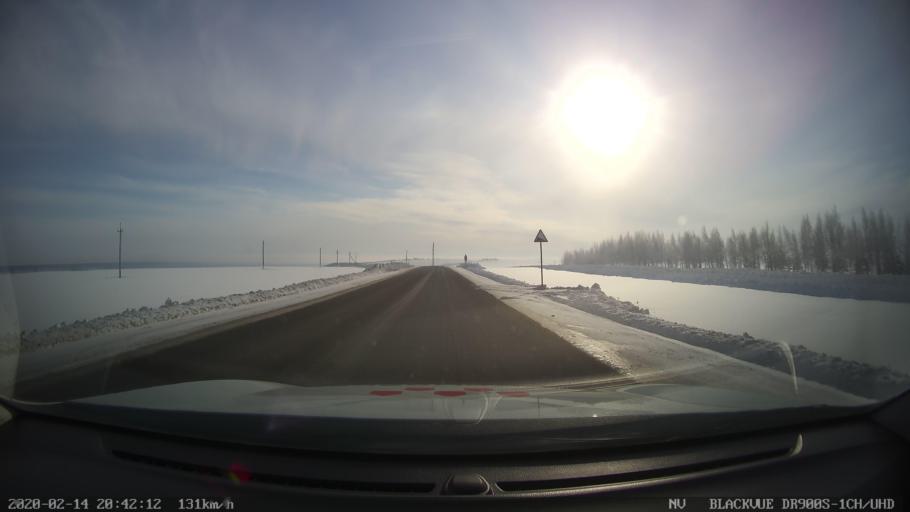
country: RU
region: Tatarstan
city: Kuybyshevskiy Zaton
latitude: 55.3196
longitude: 49.1385
